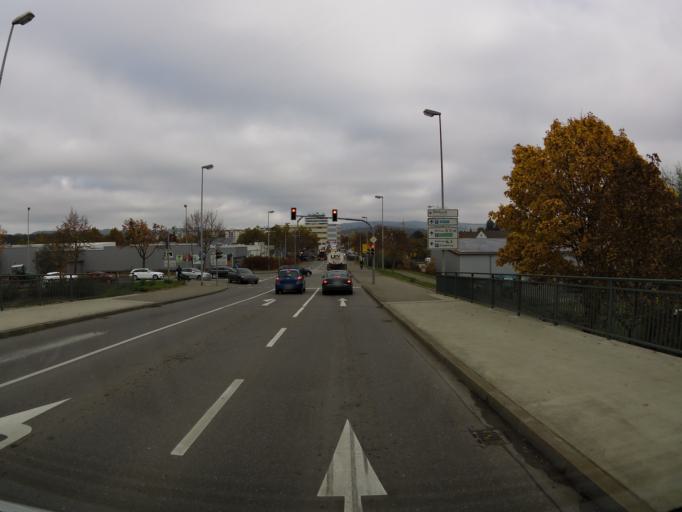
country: DE
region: Baden-Wuerttemberg
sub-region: Freiburg Region
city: Radolfzell am Bodensee
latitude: 47.7414
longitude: 8.9561
